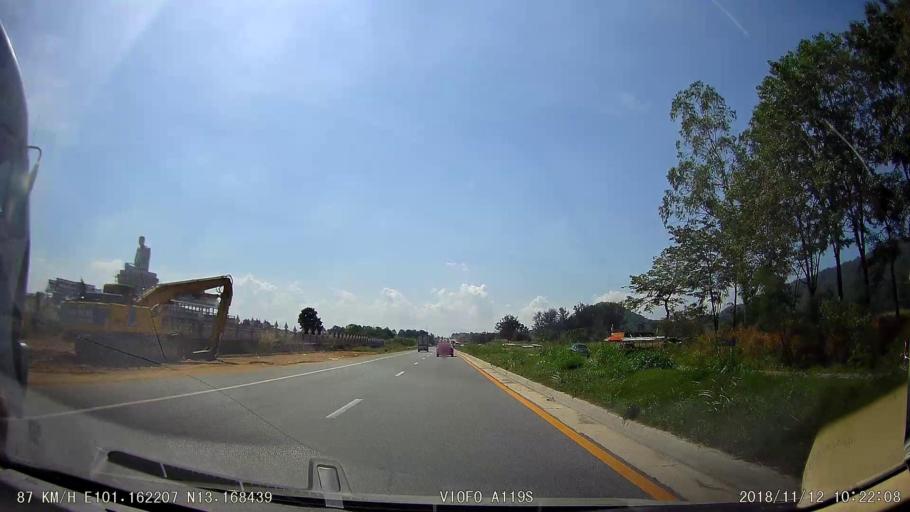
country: TH
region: Chon Buri
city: Ban Bueng
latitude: 13.1681
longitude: 101.1621
